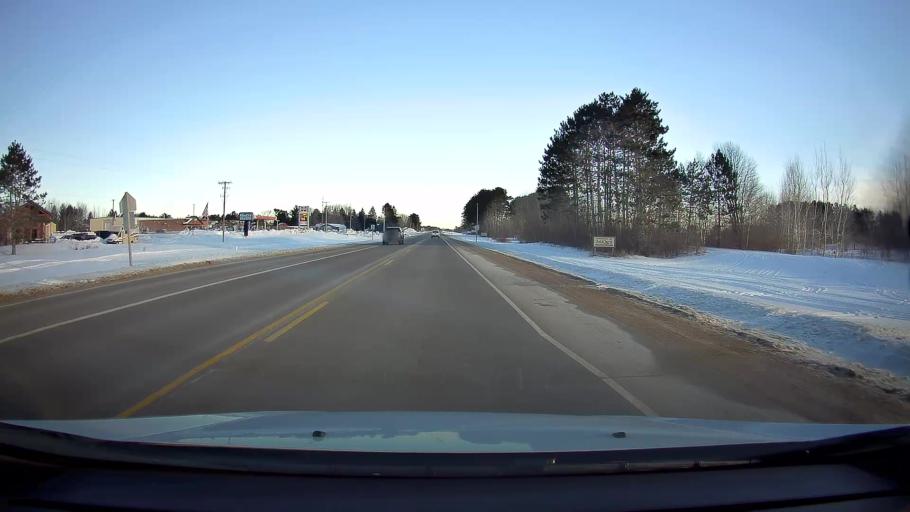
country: US
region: Wisconsin
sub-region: Washburn County
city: Shell Lake
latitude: 45.7321
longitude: -91.9303
